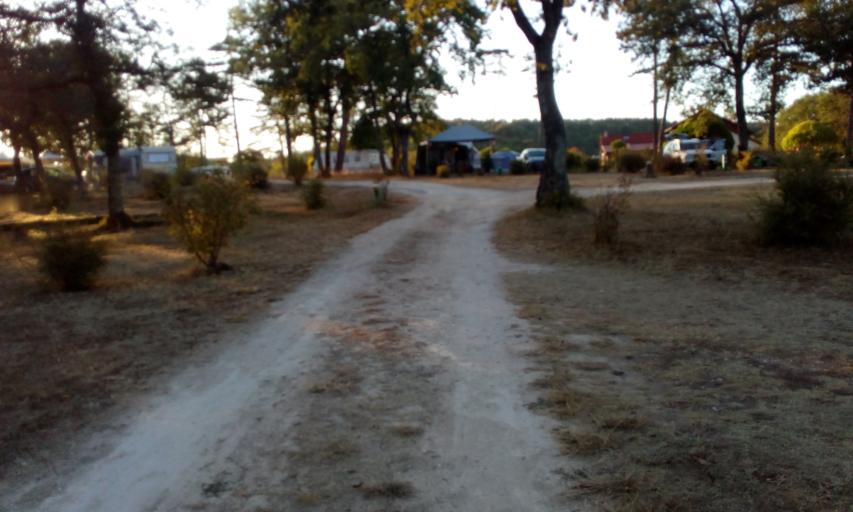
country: FR
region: Lorraine
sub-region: Departement de Meurthe-et-Moselle
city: Pagny-sur-Moselle
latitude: 48.9649
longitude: 5.8856
